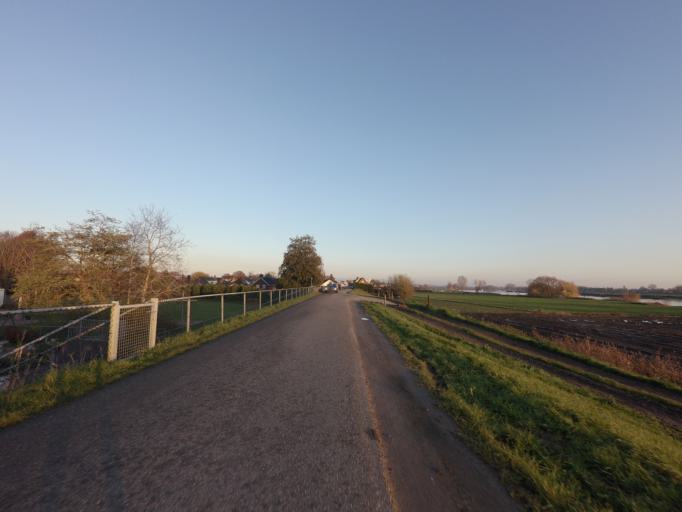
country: NL
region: Gelderland
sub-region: Gemeente Maasdriel
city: Hedel
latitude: 51.7457
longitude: 5.2171
